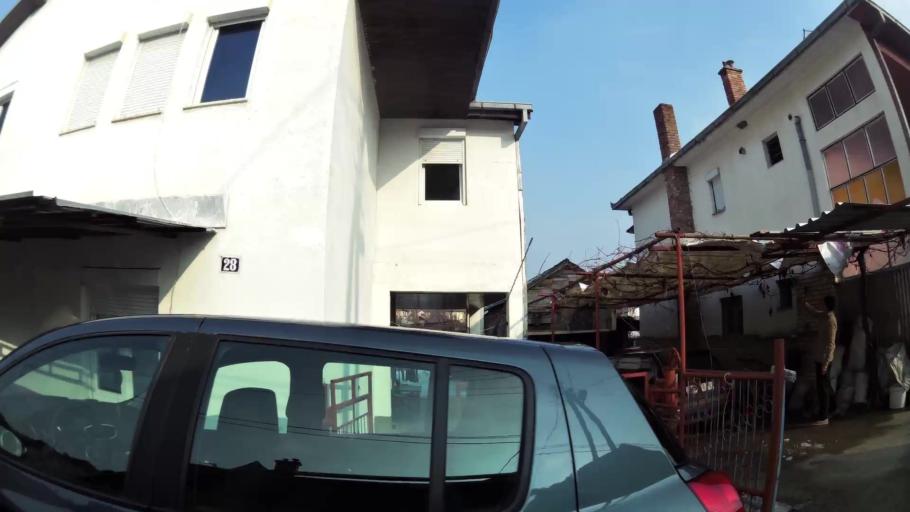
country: MK
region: Ilinden
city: Marino
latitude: 41.9880
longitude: 21.5905
